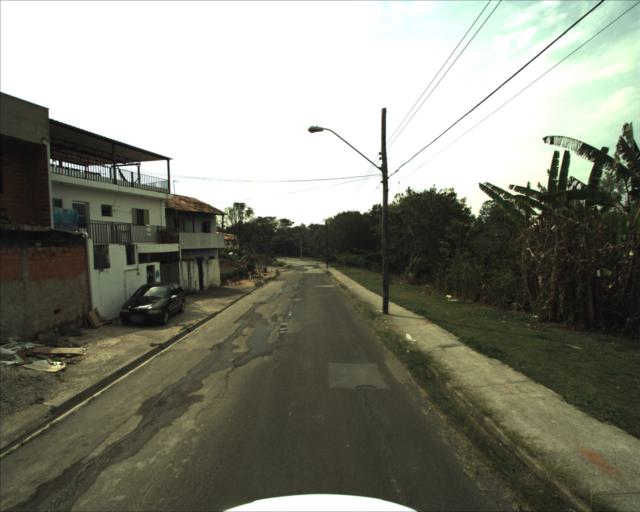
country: BR
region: Sao Paulo
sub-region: Sorocaba
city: Sorocaba
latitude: -23.4978
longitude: -47.5205
